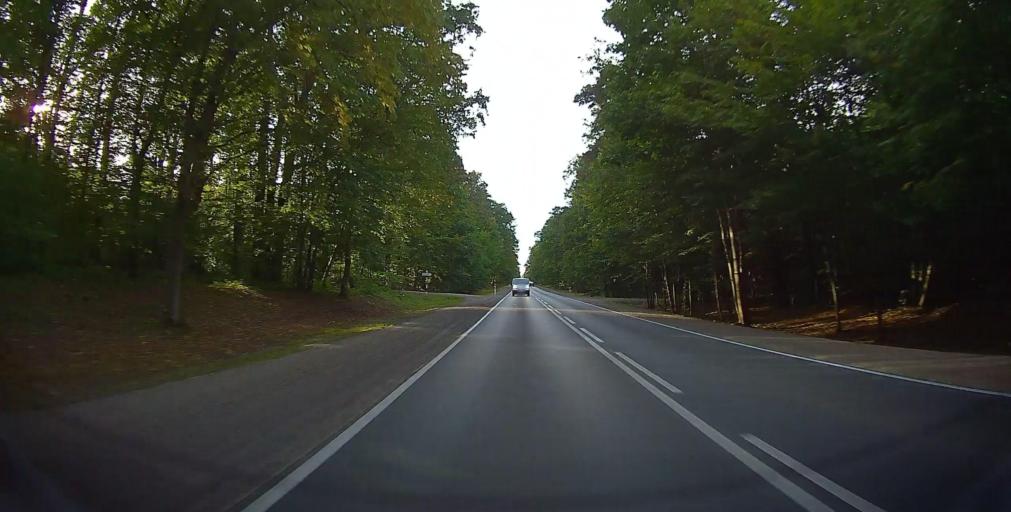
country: PL
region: Masovian Voivodeship
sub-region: Powiat piaseczynski
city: Zabieniec
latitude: 52.0463
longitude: 21.0746
